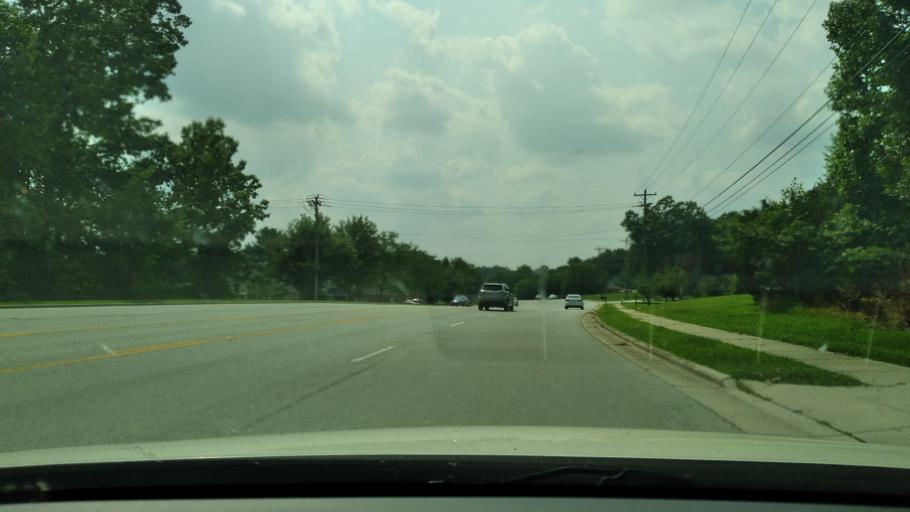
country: US
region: North Carolina
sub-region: Guilford County
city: Jamestown
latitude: 36.0387
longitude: -79.9089
